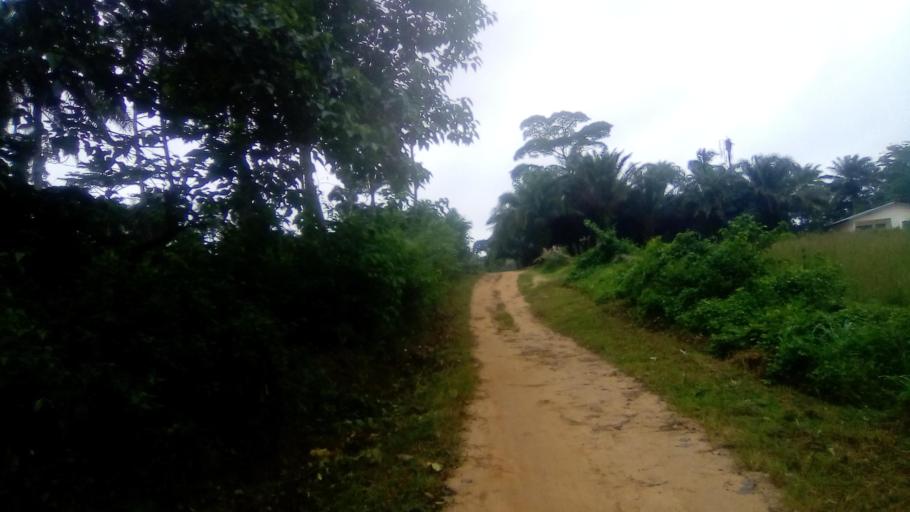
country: SL
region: Eastern Province
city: Kailahun
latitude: 8.2952
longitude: -10.6042
